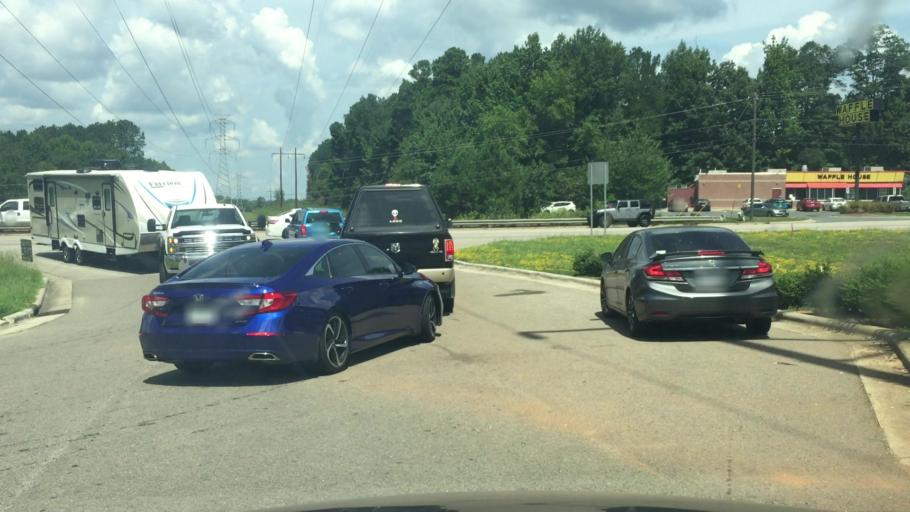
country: US
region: North Carolina
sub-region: Richmond County
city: East Rockingham
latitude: 34.9118
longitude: -79.7903
